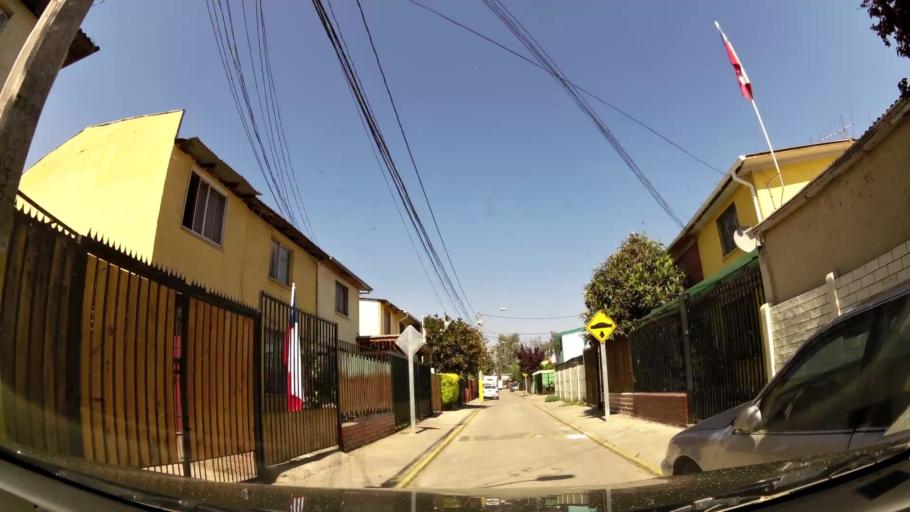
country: CL
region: Santiago Metropolitan
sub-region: Provincia de Santiago
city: Lo Prado
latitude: -33.3637
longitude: -70.7461
